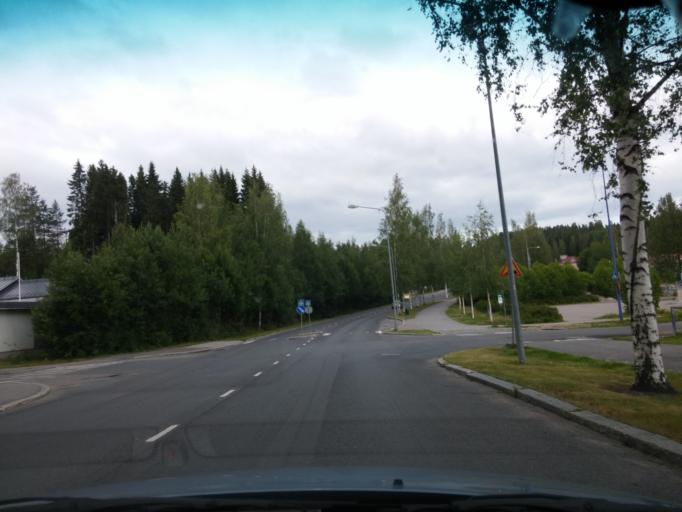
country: FI
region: Northern Savo
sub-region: Kuopio
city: Kuopio
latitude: 62.8398
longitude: 27.6566
